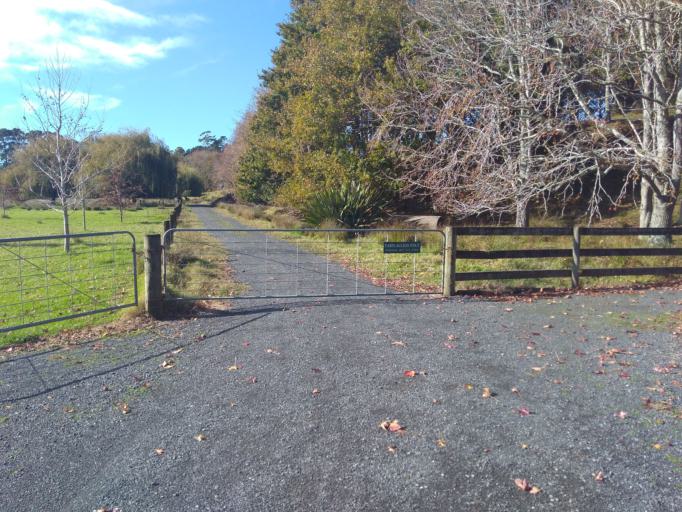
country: NZ
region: Auckland
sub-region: Auckland
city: Pakuranga
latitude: -36.9169
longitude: 174.9719
